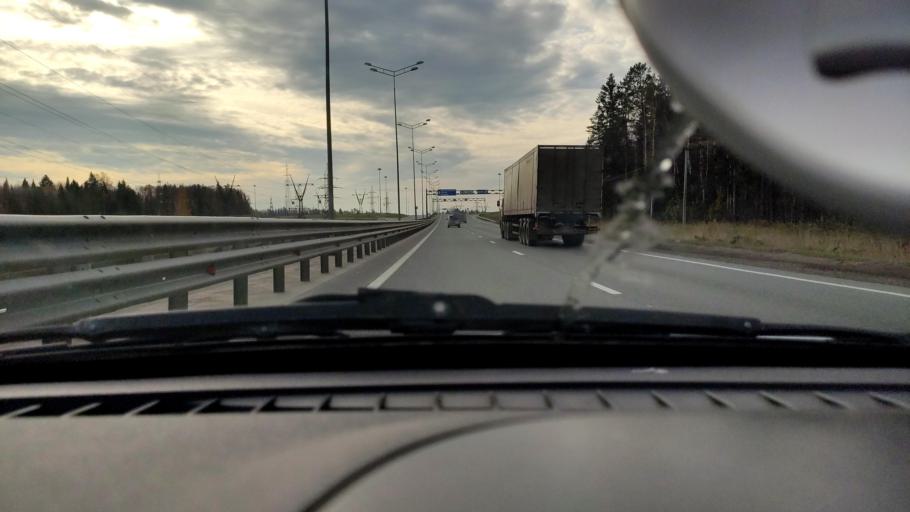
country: RU
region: Perm
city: Novyye Lyady
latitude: 58.0518
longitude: 56.4284
